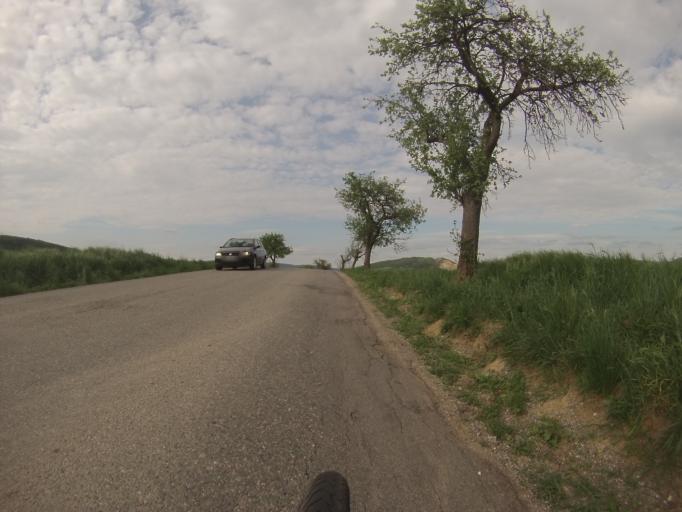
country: CZ
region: South Moravian
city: Cebin
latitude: 49.2994
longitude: 16.4590
